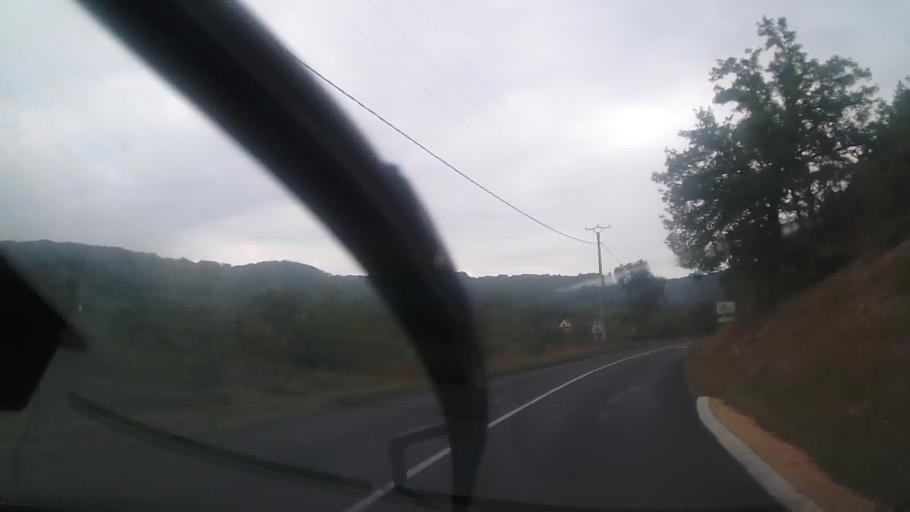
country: FR
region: Aquitaine
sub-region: Departement de la Dordogne
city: Cenac-et-Saint-Julien
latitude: 44.7890
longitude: 1.1760
